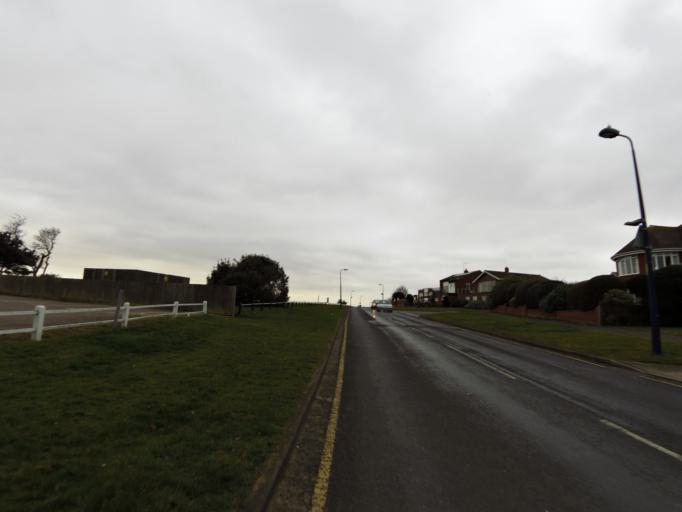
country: GB
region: England
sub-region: Suffolk
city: Felixstowe
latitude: 51.9771
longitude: 1.3802
